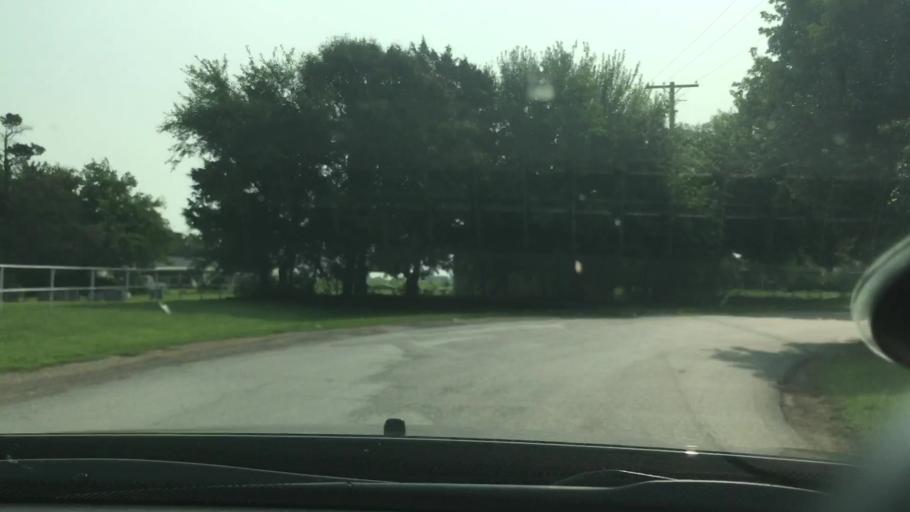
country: US
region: Oklahoma
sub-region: Garvin County
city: Lindsay
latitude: 34.8123
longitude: -97.5998
